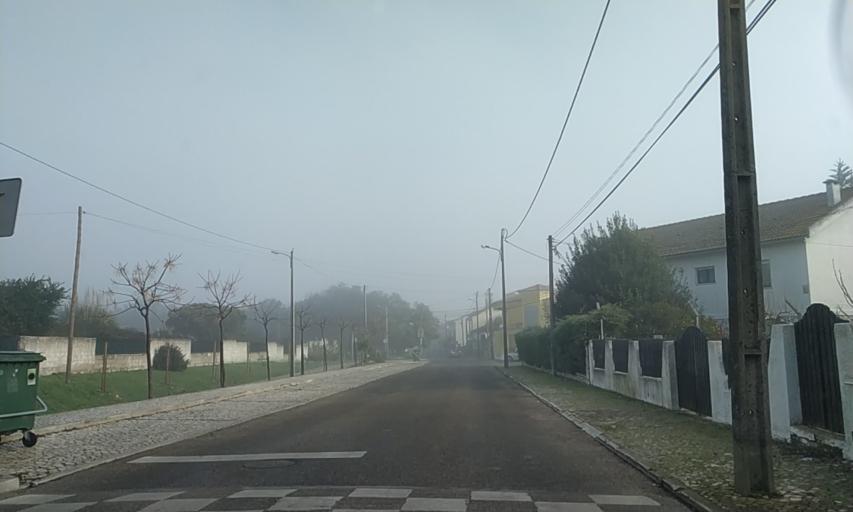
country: PT
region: Setubal
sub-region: Palmela
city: Pinhal Novo
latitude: 38.6381
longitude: -8.9168
